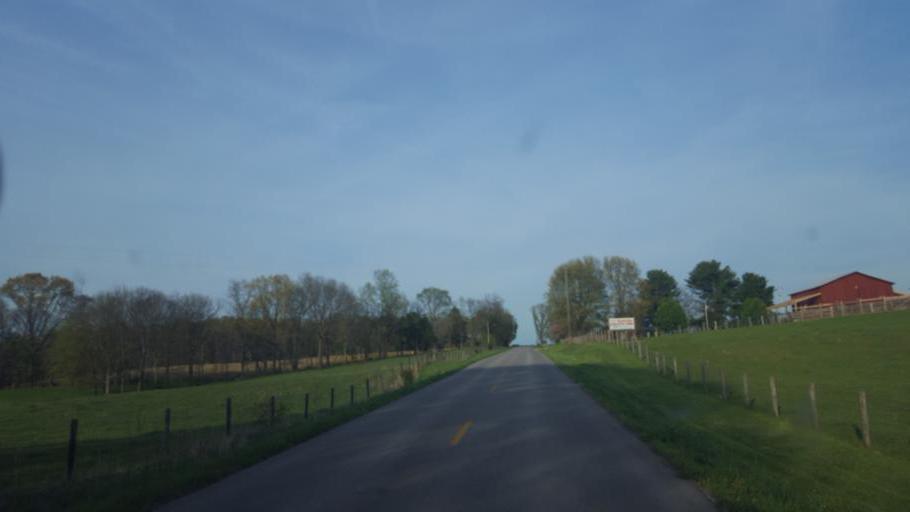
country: US
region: Kentucky
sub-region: Barren County
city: Glasgow
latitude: 36.9396
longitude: -86.0639
